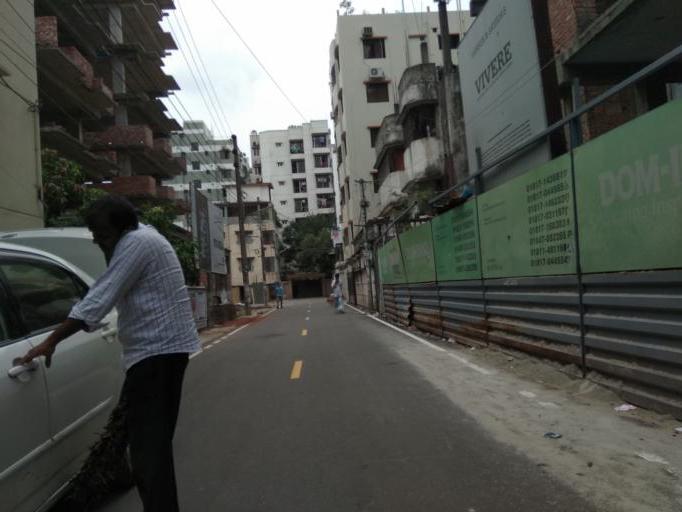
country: BD
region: Dhaka
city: Tungi
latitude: 23.8219
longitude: 90.3633
